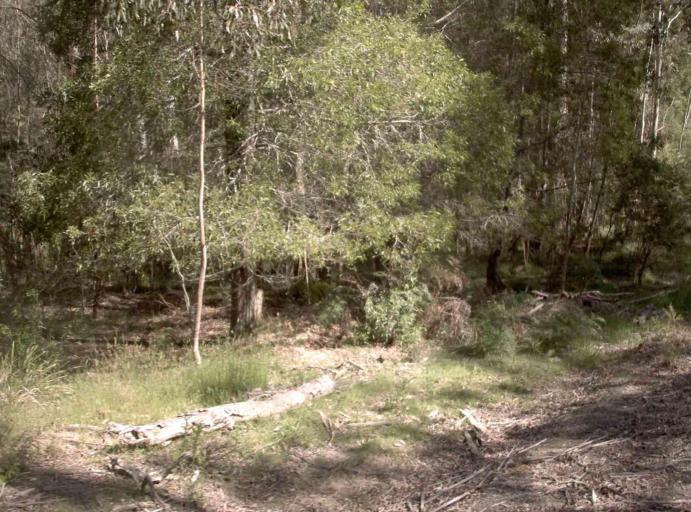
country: AU
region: New South Wales
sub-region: Bombala
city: Bombala
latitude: -37.1538
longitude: 148.7246
